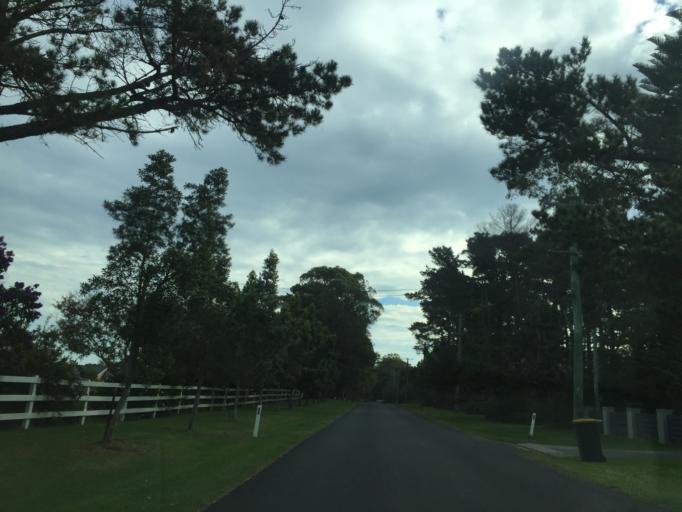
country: AU
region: New South Wales
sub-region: Hornsby Shire
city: Galston
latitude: -33.6469
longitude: 151.0731
